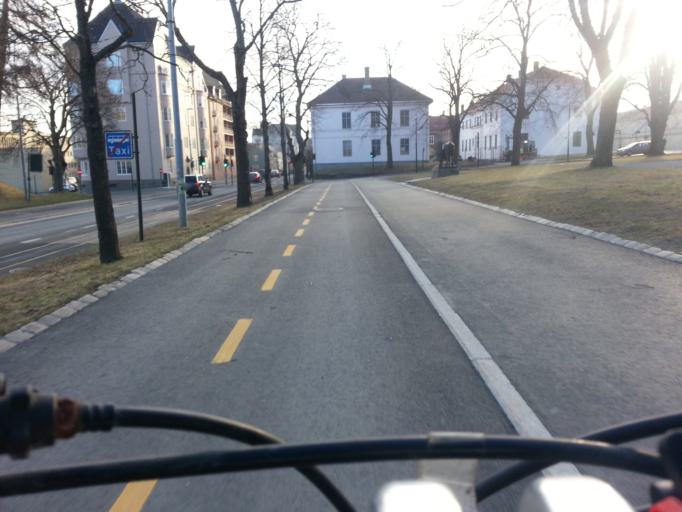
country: NO
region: Sor-Trondelag
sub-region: Trondheim
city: Trondheim
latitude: 63.4302
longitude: 10.3762
